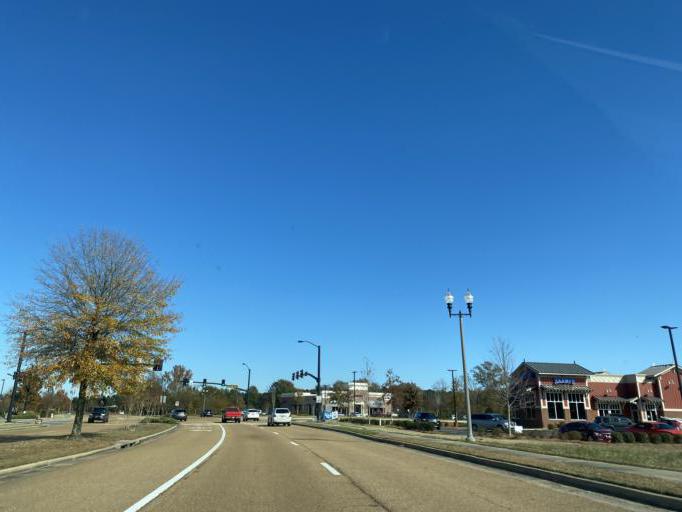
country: US
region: Mississippi
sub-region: Madison County
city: Madison
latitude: 32.4619
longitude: -90.1349
